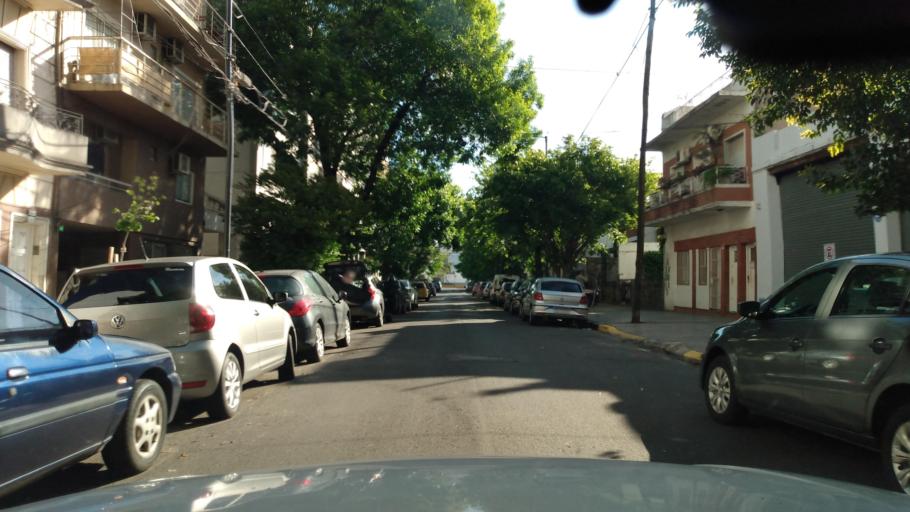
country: AR
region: Buenos Aires
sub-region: Partido de General San Martin
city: General San Martin
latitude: -34.5794
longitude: -58.4929
